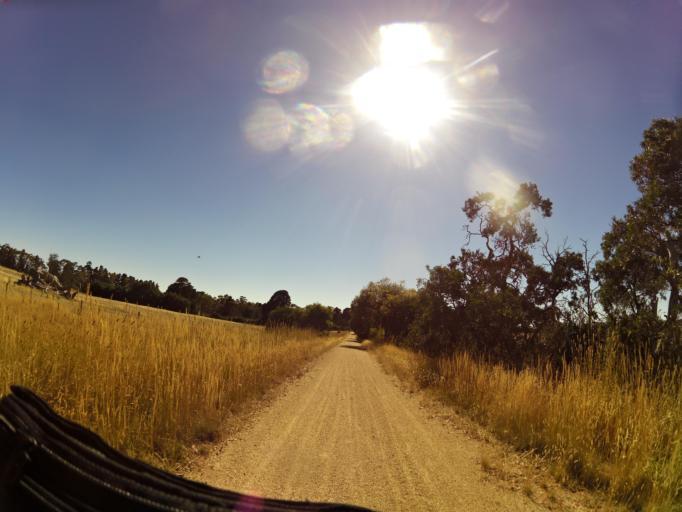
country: AU
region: Victoria
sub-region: Ballarat North
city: Delacombe
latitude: -37.6827
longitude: 143.4246
